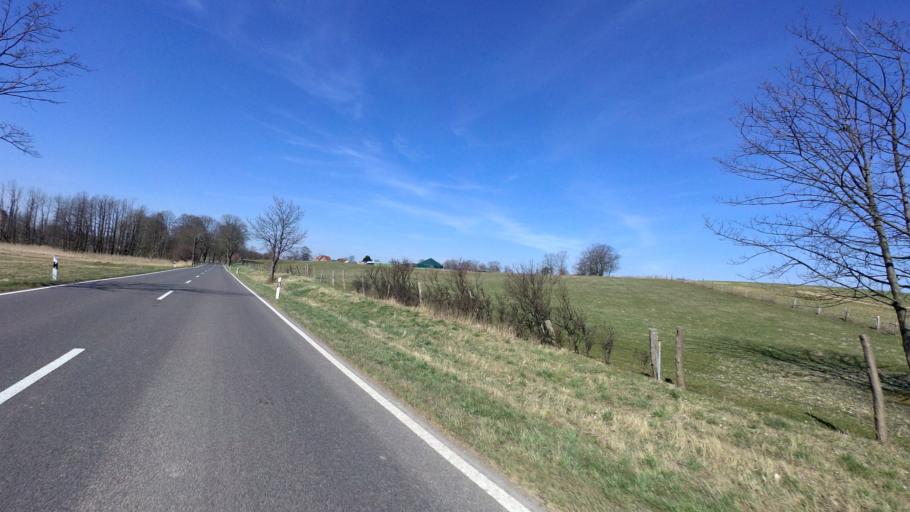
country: DE
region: Brandenburg
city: Protzel
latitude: 52.6246
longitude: 14.0164
